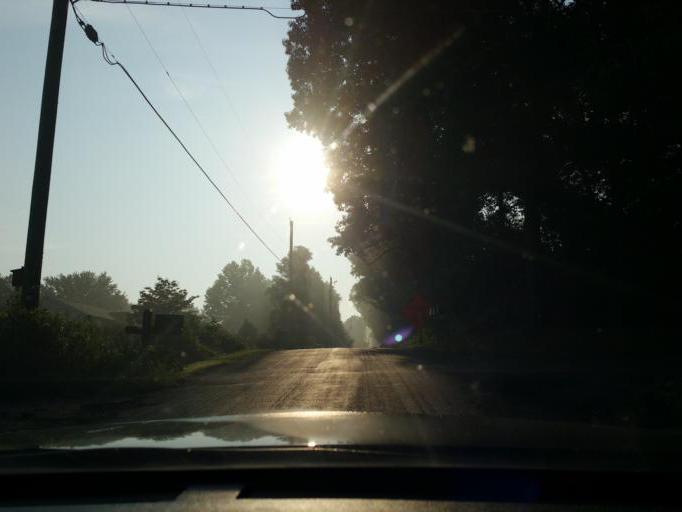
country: US
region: Maryland
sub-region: Cecil County
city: Rising Sun
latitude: 39.7180
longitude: -76.1096
